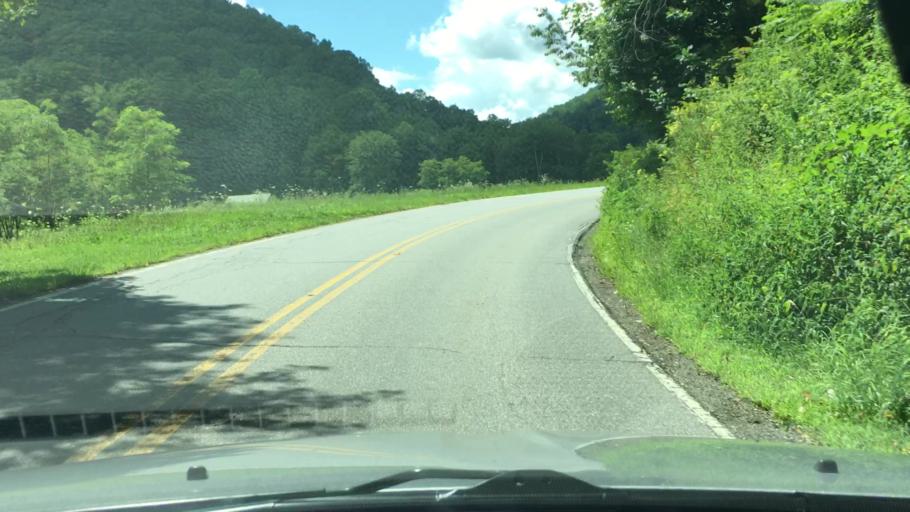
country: US
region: North Carolina
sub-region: Madison County
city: Mars Hill
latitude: 35.9352
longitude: -82.5317
